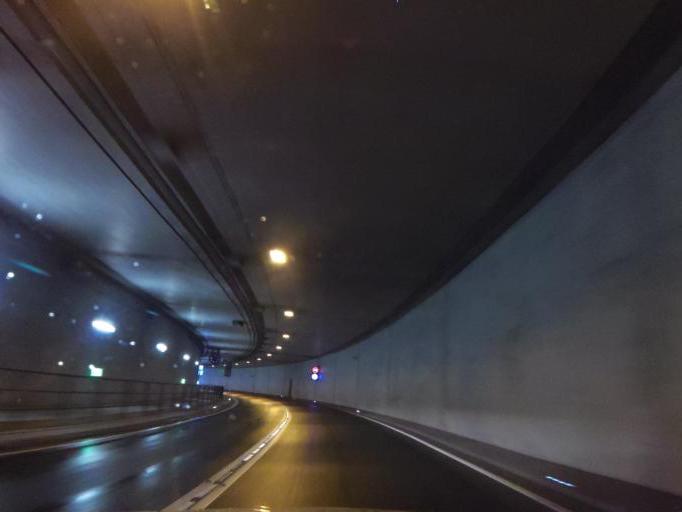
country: DE
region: Hesse
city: Kelsterbach
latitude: 50.0411
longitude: 8.5156
